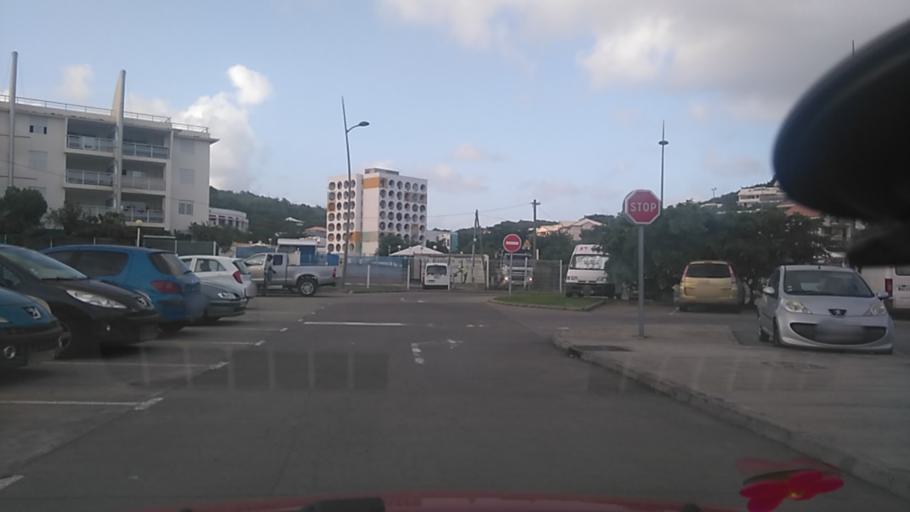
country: MQ
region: Martinique
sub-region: Martinique
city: Le Marin
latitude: 14.4695
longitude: -60.8643
